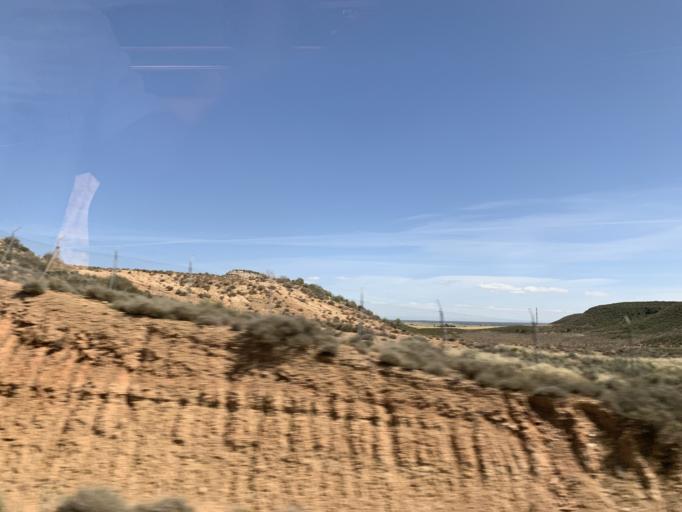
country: ES
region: Aragon
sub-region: Provincia de Huesca
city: Candasnos
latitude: 41.5300
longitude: 0.0356
